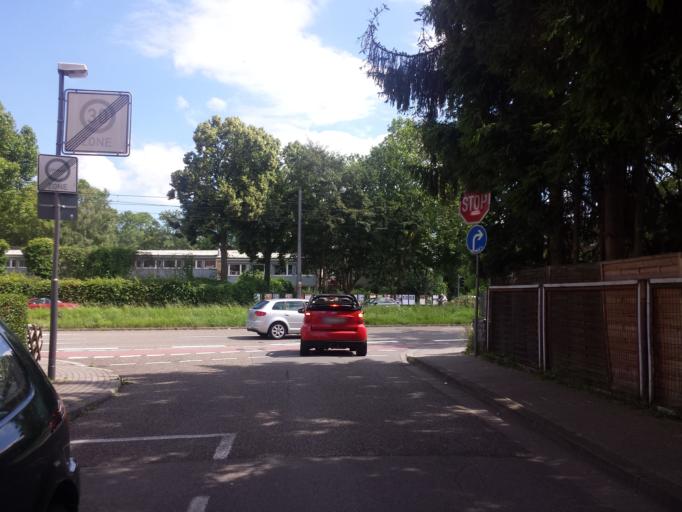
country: DE
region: Baden-Wuerttemberg
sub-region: Karlsruhe Region
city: Heidelberg
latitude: 49.4243
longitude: 8.6801
